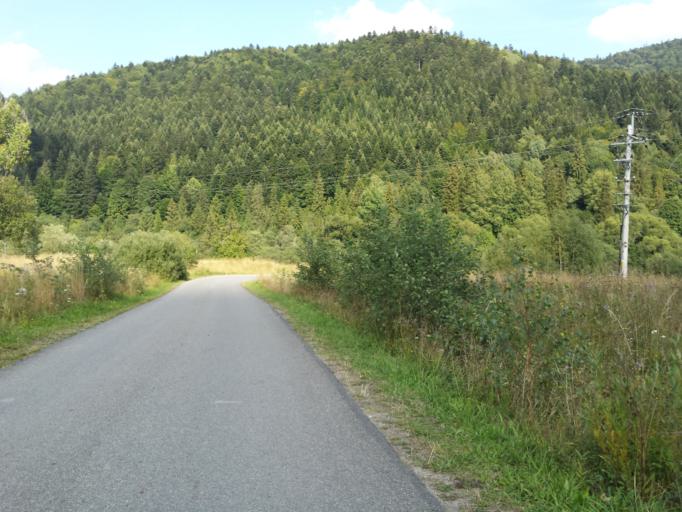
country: PL
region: Subcarpathian Voivodeship
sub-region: Powiat leski
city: Cisna
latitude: 49.1973
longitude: 22.3656
